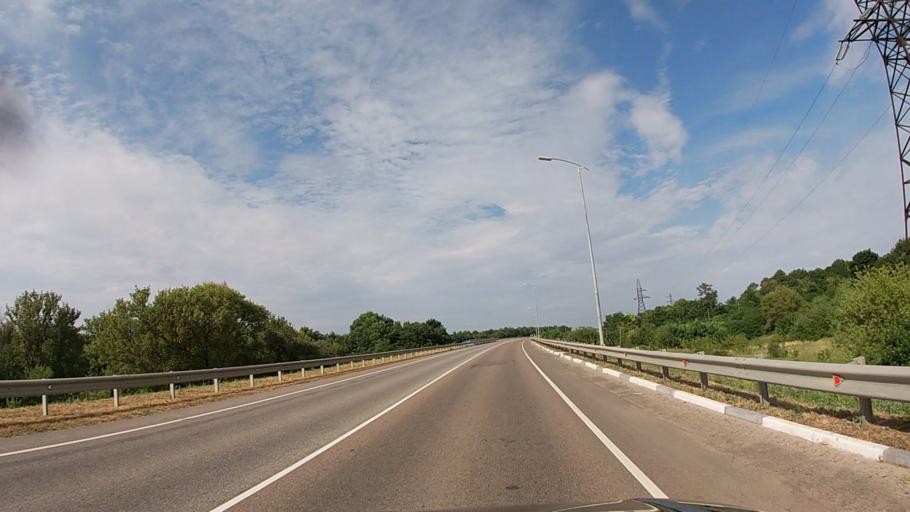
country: RU
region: Belgorod
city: Proletarskiy
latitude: 50.8040
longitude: 35.7392
